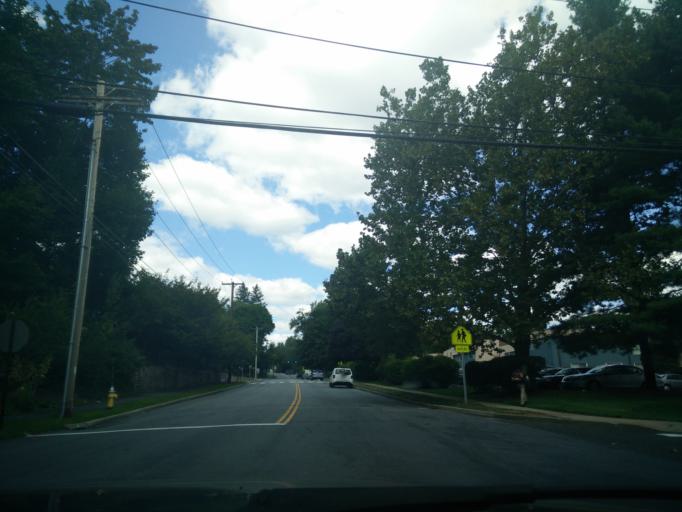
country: US
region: Connecticut
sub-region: Fairfield County
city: Bridgeport
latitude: 41.1948
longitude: -73.2362
